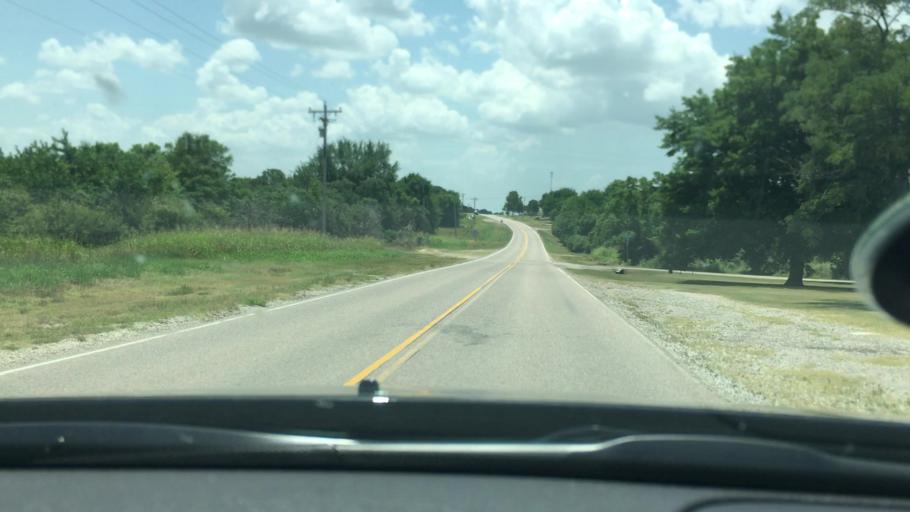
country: US
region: Oklahoma
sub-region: Johnston County
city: Tishomingo
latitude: 34.4482
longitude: -96.6363
